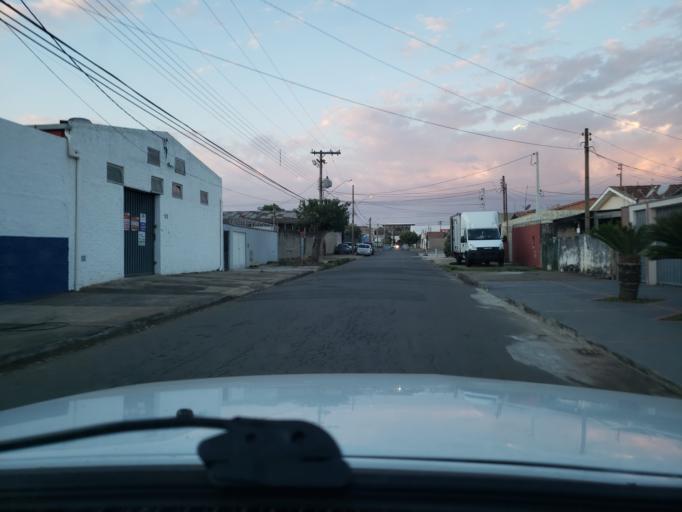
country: BR
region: Sao Paulo
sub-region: Moji-Guacu
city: Mogi-Gaucu
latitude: -22.3474
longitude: -46.9512
